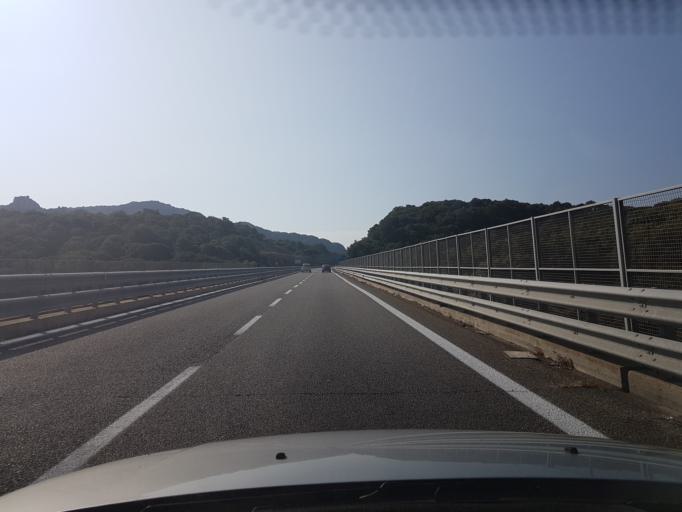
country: IT
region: Sardinia
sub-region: Provincia di Olbia-Tempio
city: Padru
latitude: 40.8131
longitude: 9.5868
